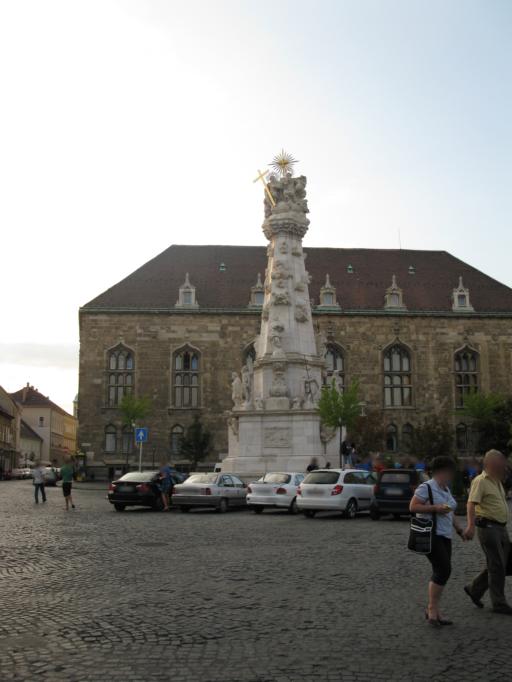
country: HU
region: Budapest
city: Budapest
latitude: 47.5013
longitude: 19.0337
